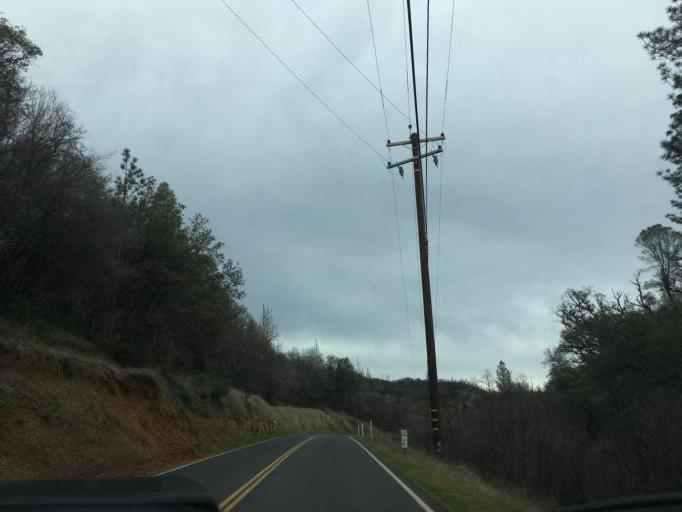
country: US
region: California
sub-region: Calaveras County
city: Mountain Ranch
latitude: 38.2307
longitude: -120.5379
